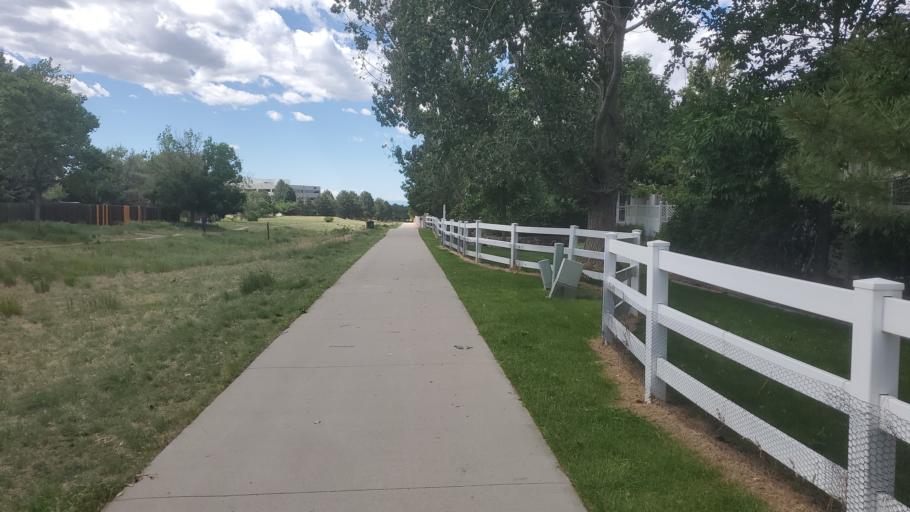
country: US
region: Colorado
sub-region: Adams County
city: Aurora
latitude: 39.6707
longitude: -104.8420
